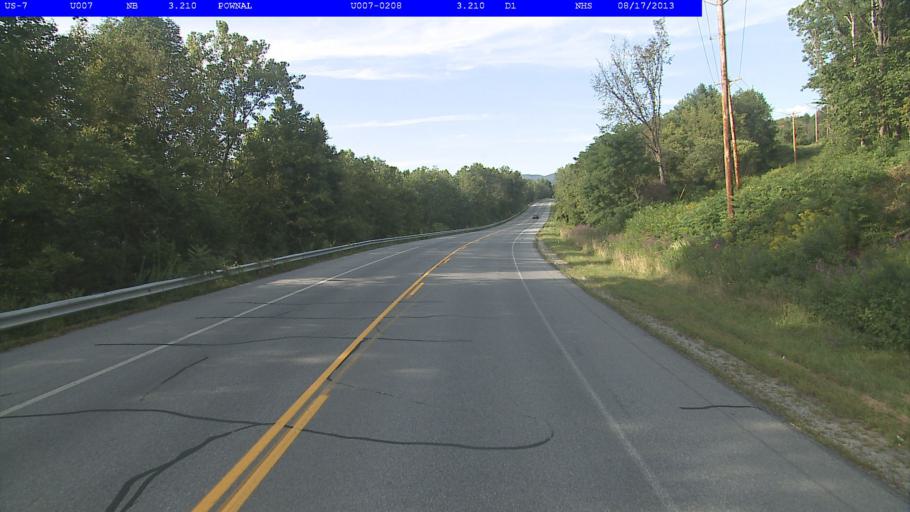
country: US
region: Massachusetts
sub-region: Berkshire County
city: Williamstown
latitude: 42.7811
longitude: -73.2428
